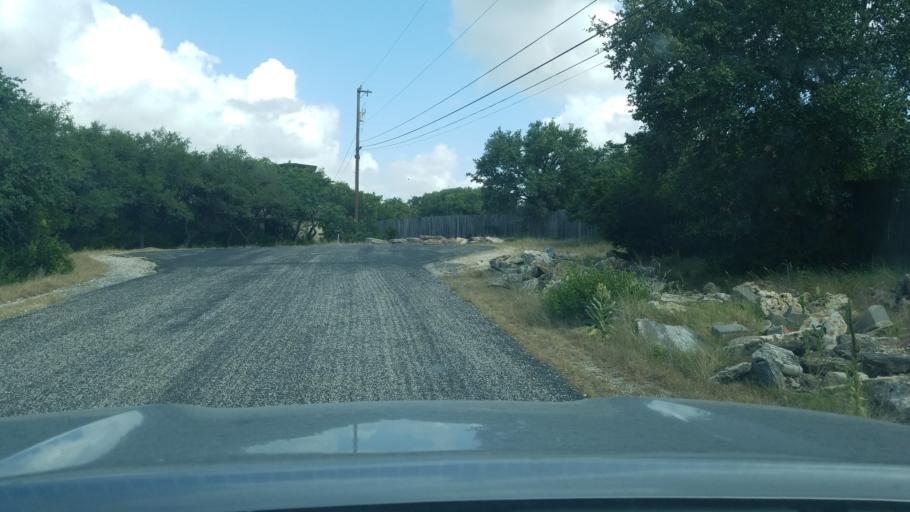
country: US
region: Texas
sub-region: Bexar County
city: Timberwood Park
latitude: 29.6894
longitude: -98.4993
